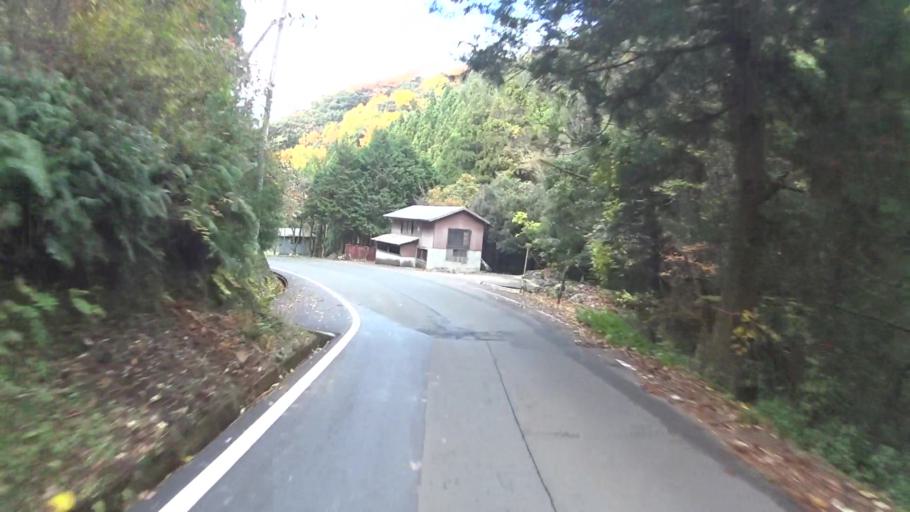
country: JP
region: Kyoto
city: Maizuru
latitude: 35.5621
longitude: 135.4352
